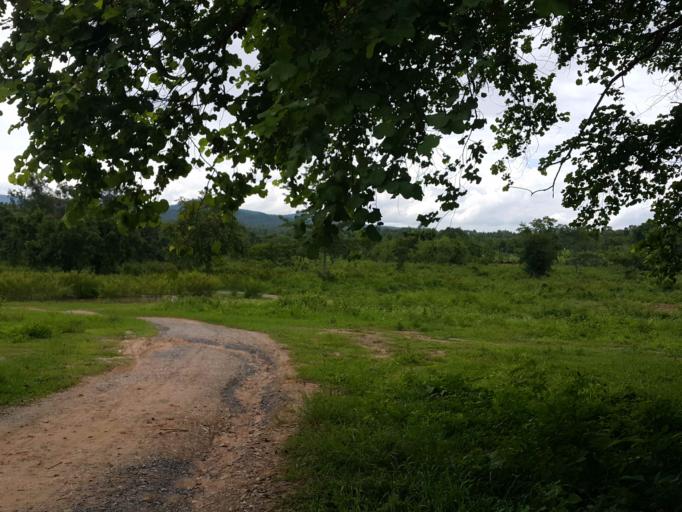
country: TH
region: Chiang Mai
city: San Sai
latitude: 18.9421
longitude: 98.9105
